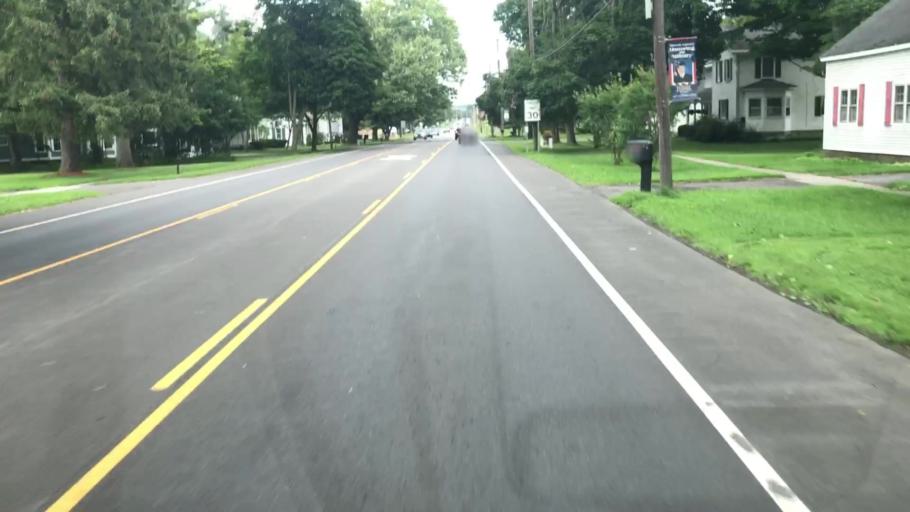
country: US
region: New York
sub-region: Onondaga County
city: Elbridge
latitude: 43.0355
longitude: -76.4422
